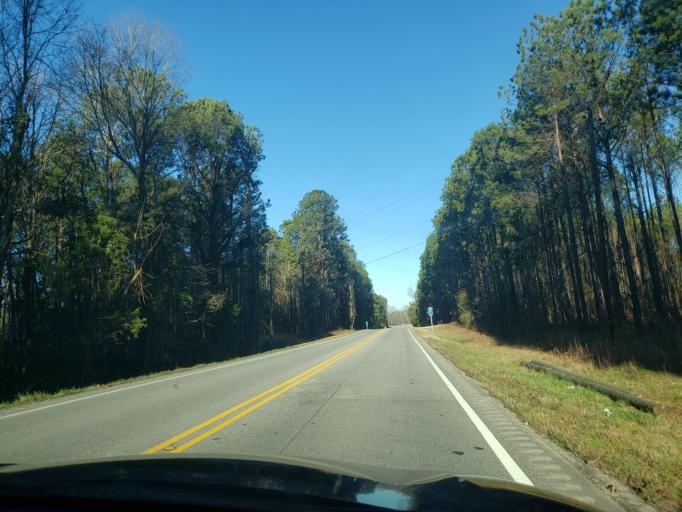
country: US
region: Alabama
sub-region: Lee County
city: Auburn
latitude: 32.5952
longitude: -85.6248
